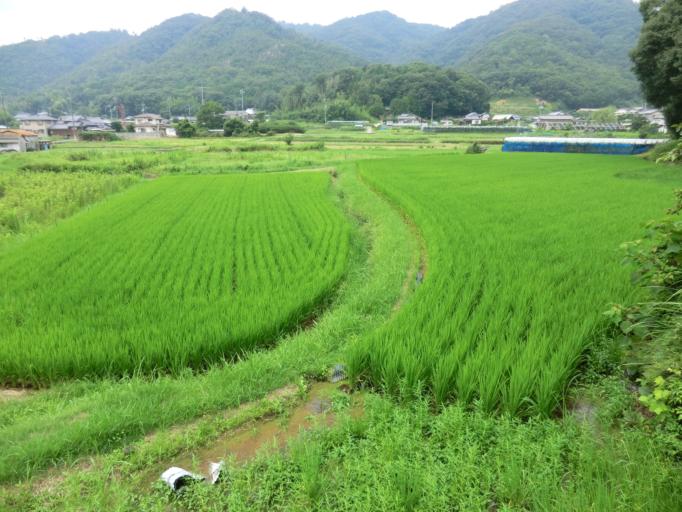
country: JP
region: Okayama
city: Okayama-shi
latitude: 34.7438
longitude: 134.0025
